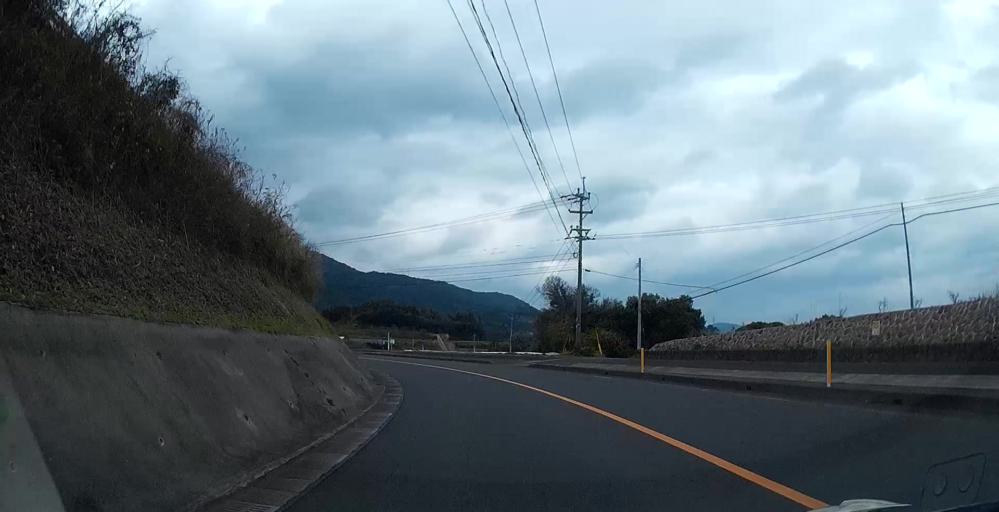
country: JP
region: Kagoshima
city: Akune
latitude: 32.1005
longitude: 130.1678
